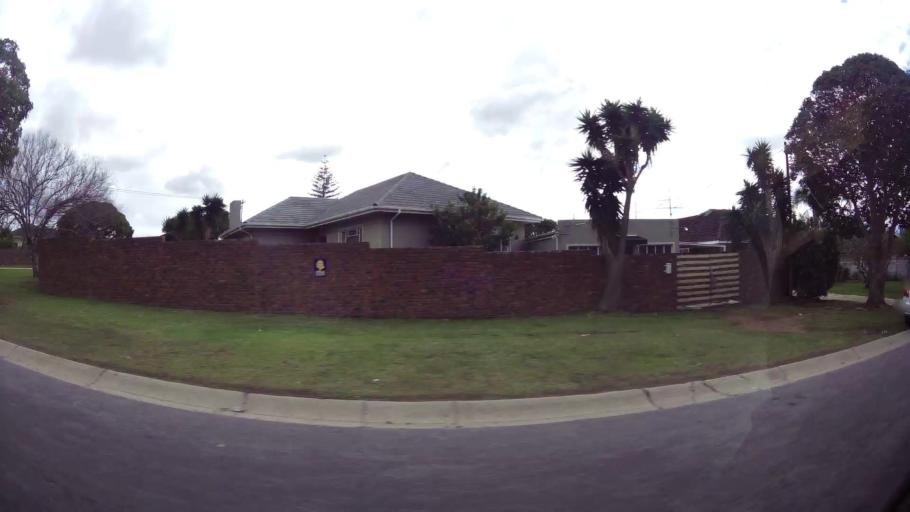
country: ZA
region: Eastern Cape
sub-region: Nelson Mandela Bay Metropolitan Municipality
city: Port Elizabeth
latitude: -33.9427
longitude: 25.5224
